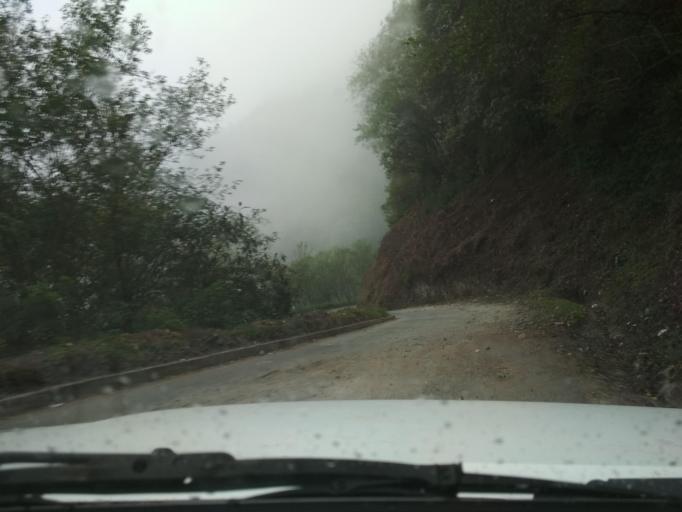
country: MX
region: Veracruz
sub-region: La Perla
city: Metlac Hernandez (Metlac Primero)
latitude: 18.9493
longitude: -97.1634
